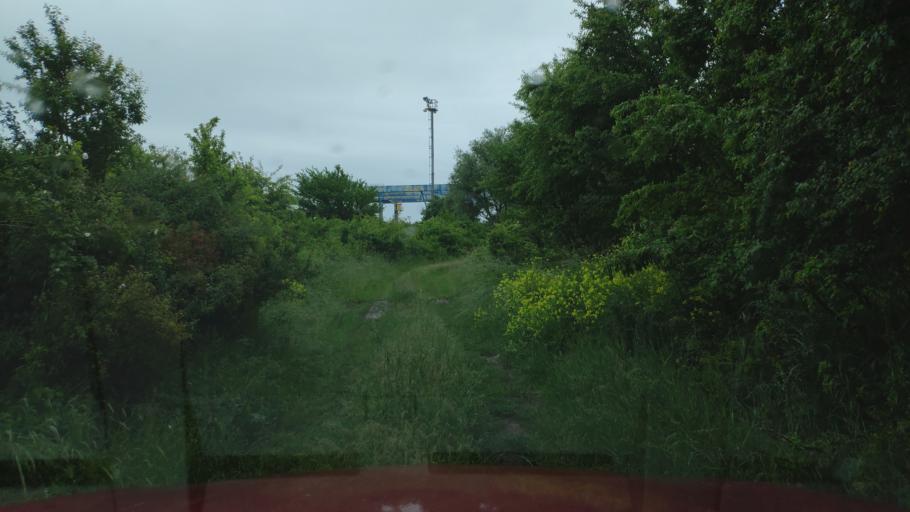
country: SK
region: Kosicky
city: Cierna nad Tisou
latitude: 48.4146
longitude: 22.0213
